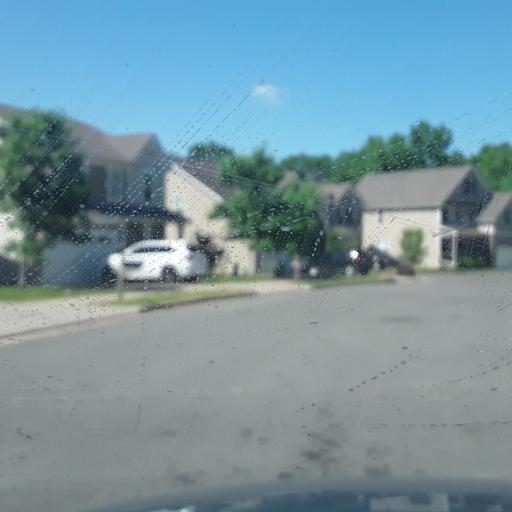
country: US
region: Tennessee
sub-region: Williamson County
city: Brentwood Estates
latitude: 36.0289
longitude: -86.7006
